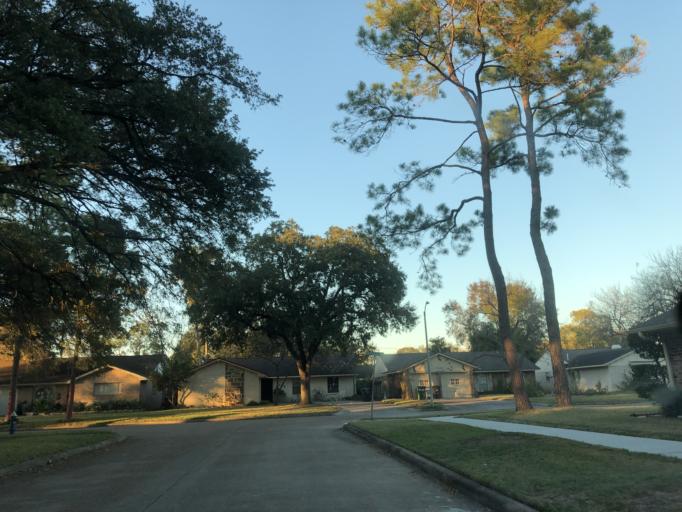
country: US
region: Texas
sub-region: Harris County
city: Bellaire
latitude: 29.6872
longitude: -95.5159
